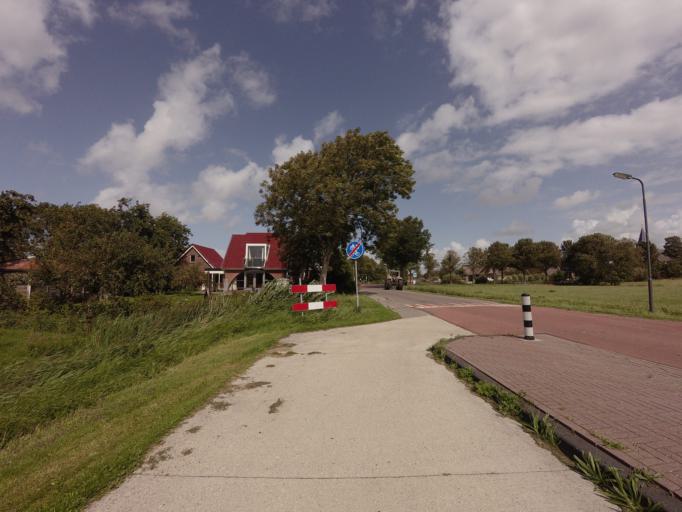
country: NL
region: Friesland
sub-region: Gemeente Harlingen
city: Harlingen
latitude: 53.1472
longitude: 5.4799
